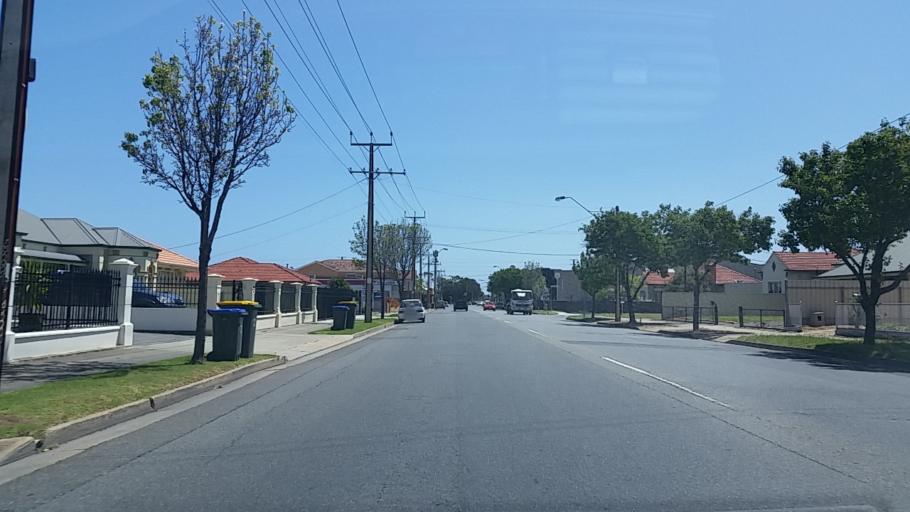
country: AU
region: South Australia
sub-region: Charles Sturt
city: Seaton
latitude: -34.8917
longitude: 138.5171
